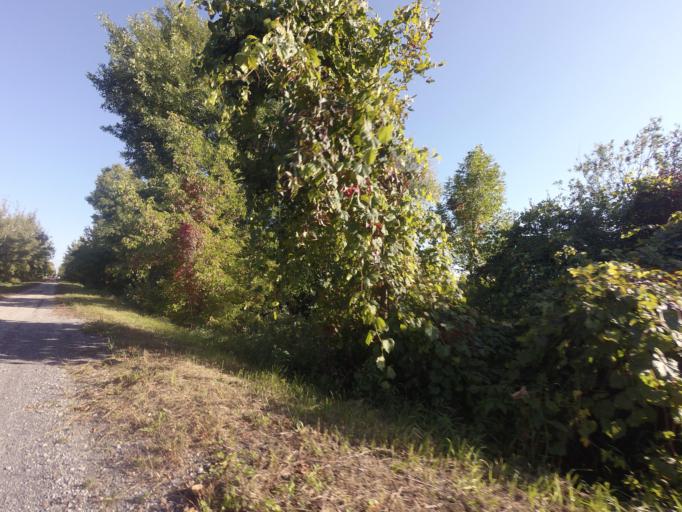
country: CA
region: Ontario
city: Hawkesbury
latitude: 45.5211
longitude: -74.5345
